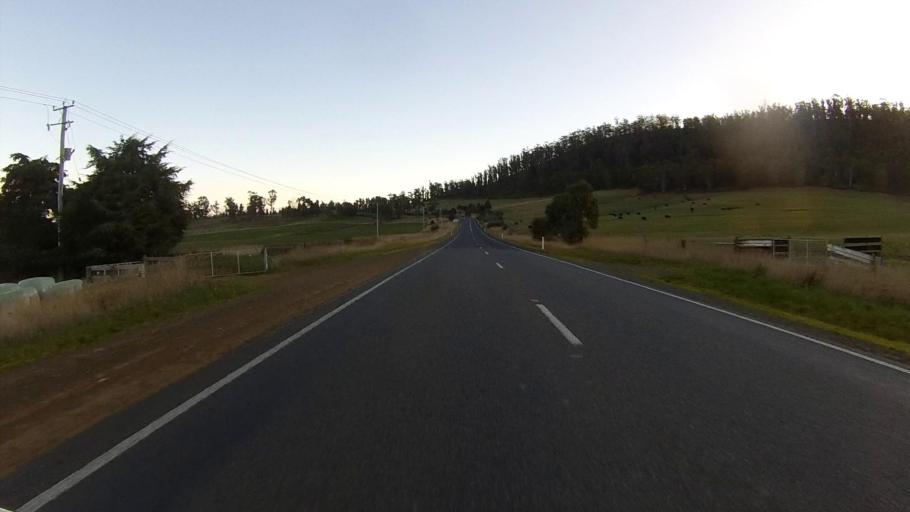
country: AU
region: Tasmania
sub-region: Sorell
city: Sorell
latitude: -42.8191
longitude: 147.7475
